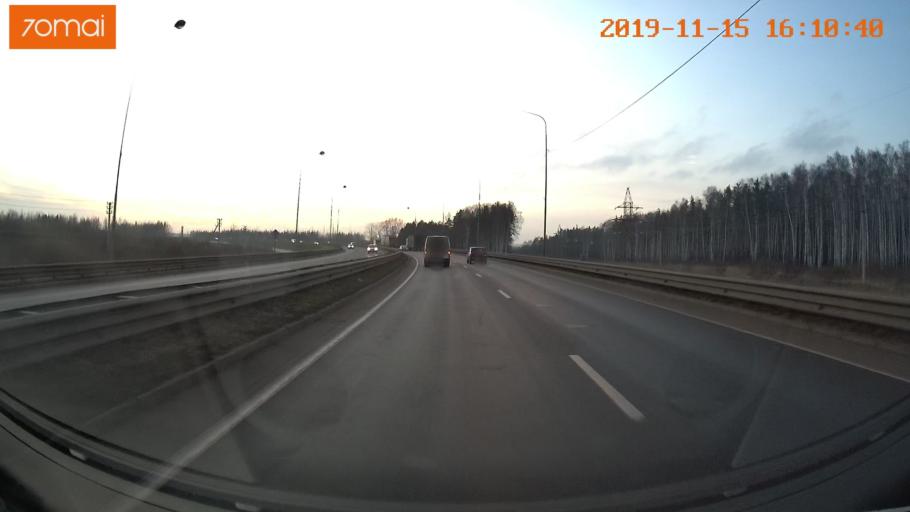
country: RU
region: Jaroslavl
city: Yaroslavl
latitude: 57.6837
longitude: 39.8813
